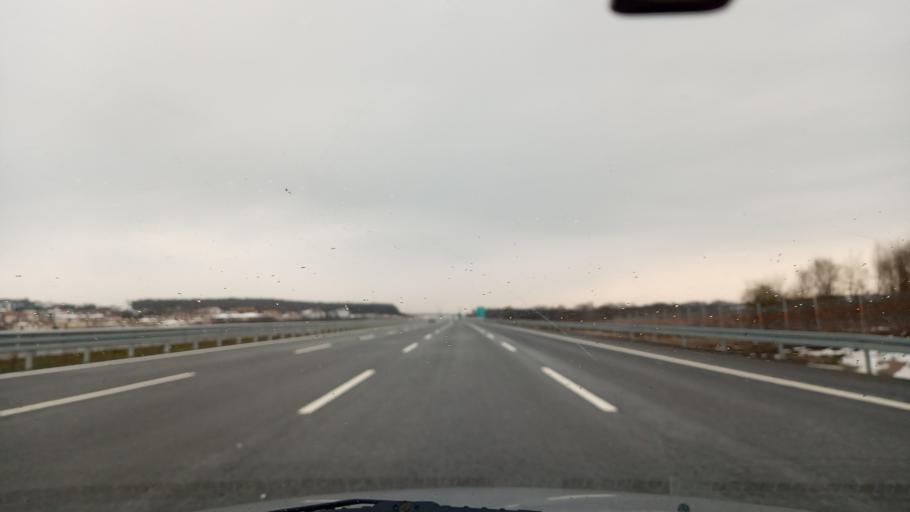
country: TR
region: Sakarya
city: Kazimpasa
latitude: 40.8451
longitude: 30.2642
